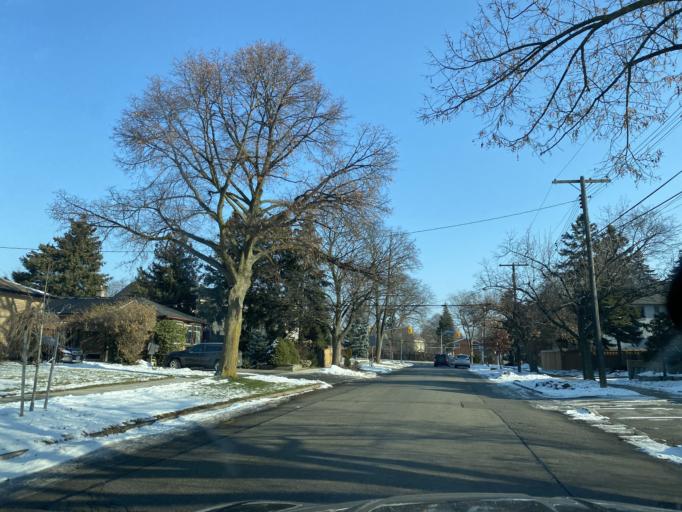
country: CA
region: Ontario
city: Etobicoke
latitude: 43.6641
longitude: -79.5598
